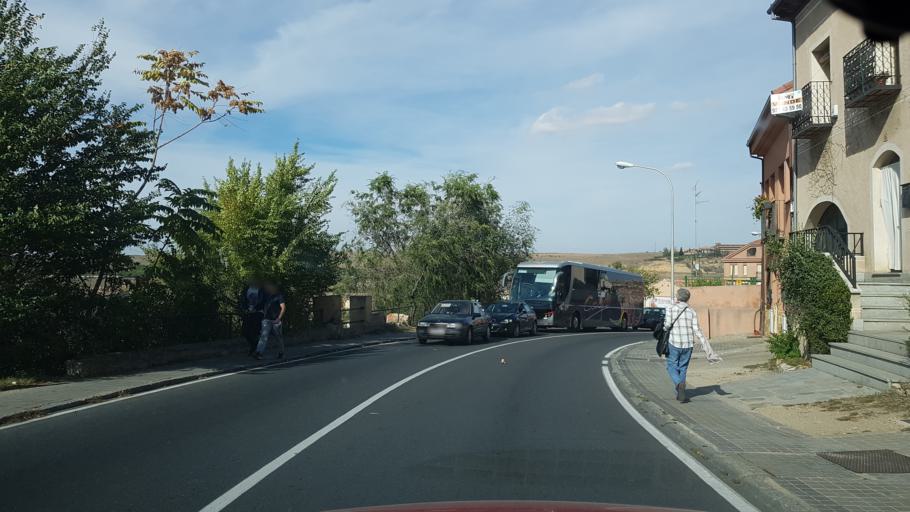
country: ES
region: Castille and Leon
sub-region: Provincia de Segovia
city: Segovia
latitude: 40.9484
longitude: -4.1132
